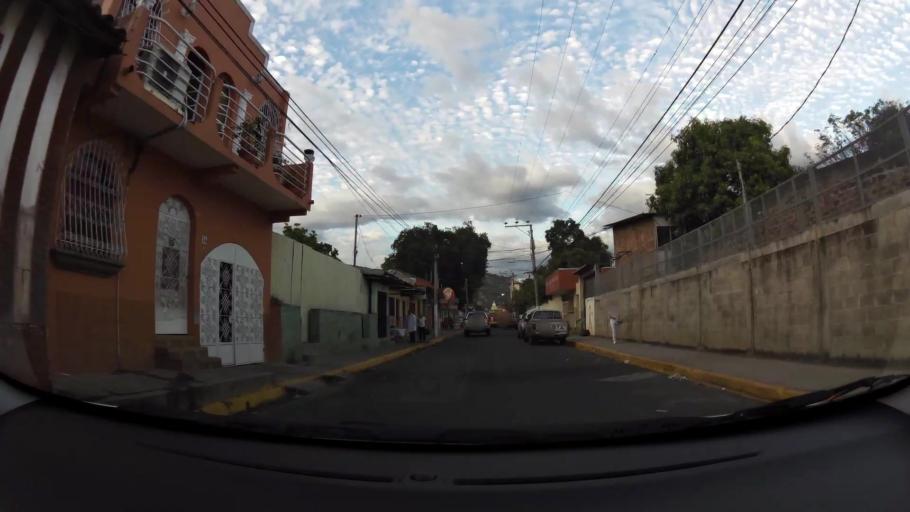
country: SV
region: San Vicente
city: San Vicente
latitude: 13.6405
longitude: -88.7848
